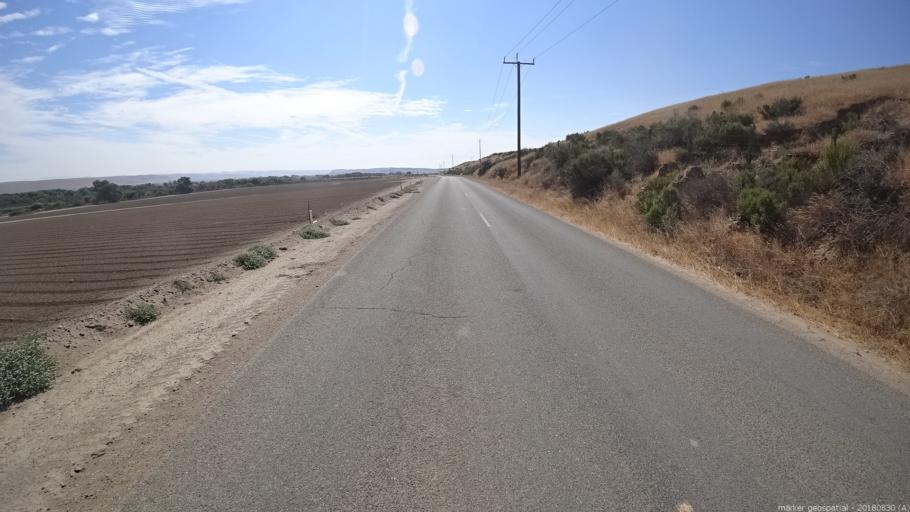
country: US
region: California
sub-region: Monterey County
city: King City
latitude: 36.1080
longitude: -121.0294
